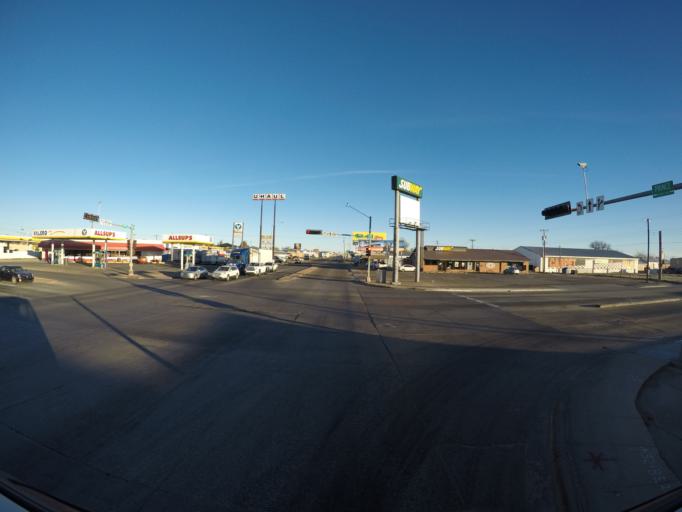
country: US
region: New Mexico
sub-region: Curry County
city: Clovis
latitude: 34.3985
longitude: -103.1964
